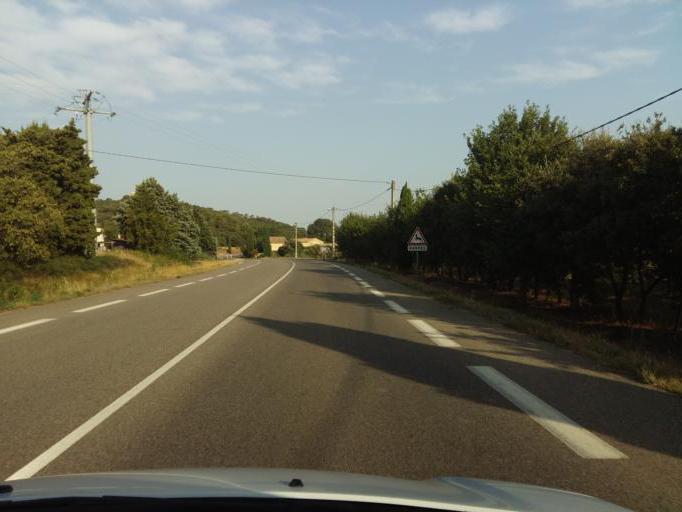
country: FR
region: Provence-Alpes-Cote d'Azur
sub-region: Departement du Vaucluse
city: Bollene
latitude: 44.2743
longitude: 4.7936
